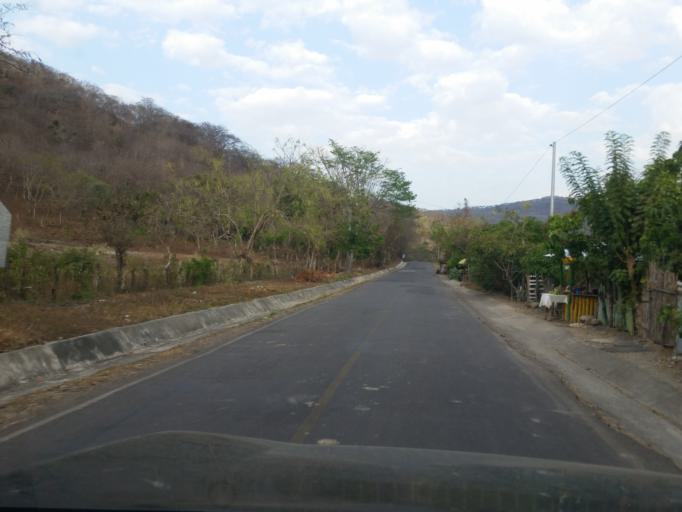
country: NI
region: Jinotega
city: La Concordia
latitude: 13.1945
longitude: -86.1551
